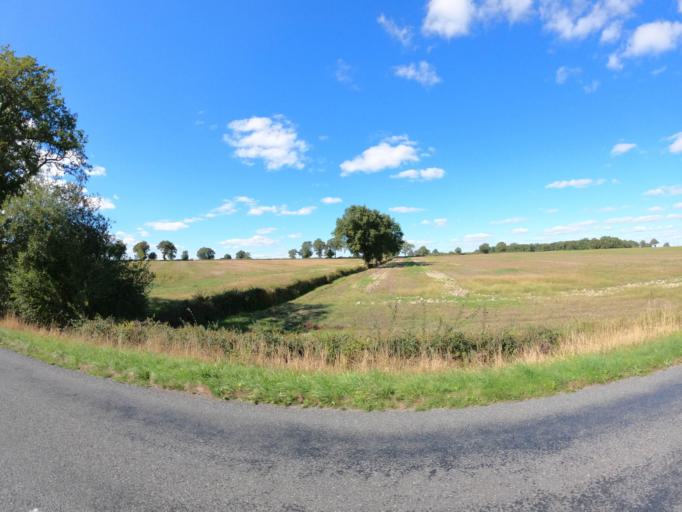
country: FR
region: Auvergne
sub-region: Departement de l'Allier
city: Doyet
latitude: 46.3868
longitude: 2.7953
